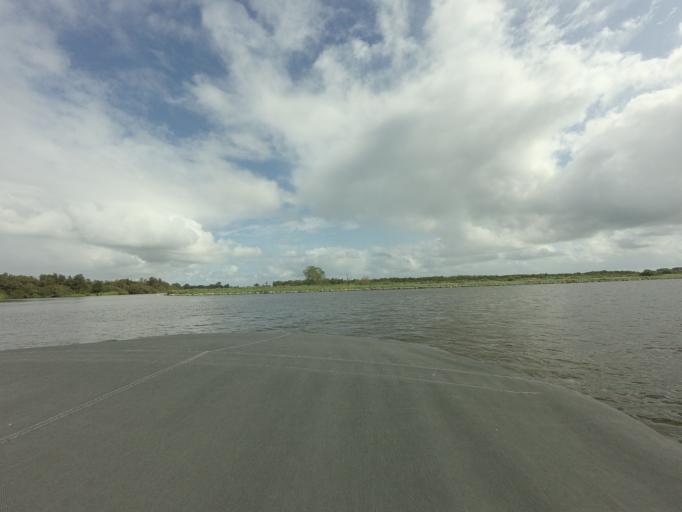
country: NL
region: Friesland
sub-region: Gemeente Boarnsterhim
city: Warten
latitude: 53.1157
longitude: 5.9355
